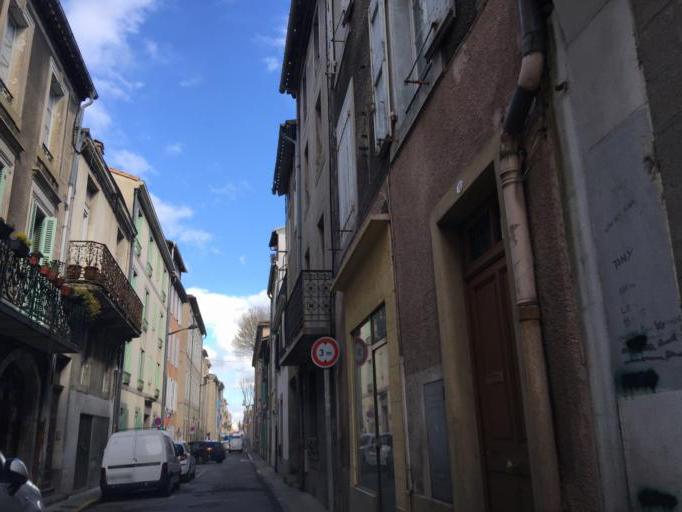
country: FR
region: Languedoc-Roussillon
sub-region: Departement de l'Aude
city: Carcassonne
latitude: 43.2149
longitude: 2.3525
